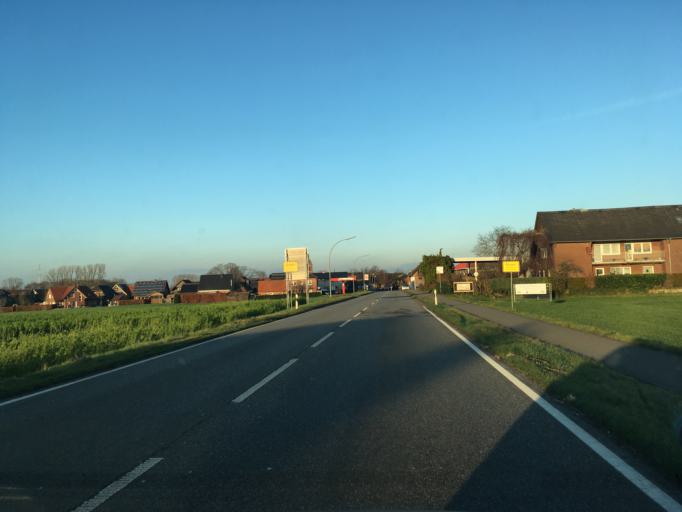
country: DE
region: North Rhine-Westphalia
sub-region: Regierungsbezirk Munster
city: Ahaus
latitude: 52.1202
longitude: 6.9869
